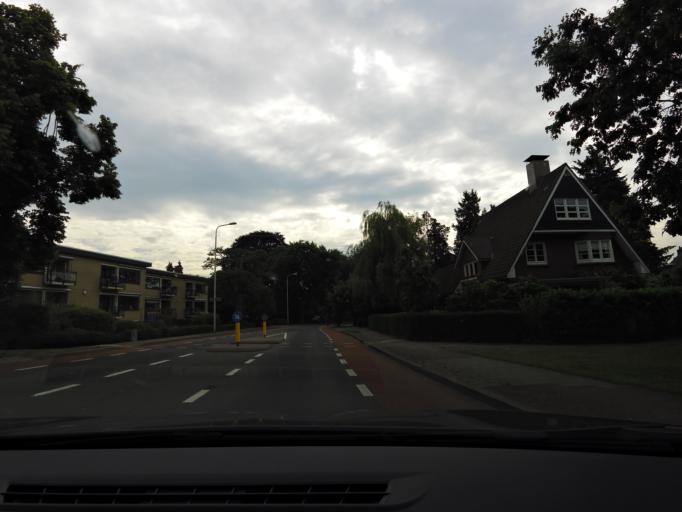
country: NL
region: Gelderland
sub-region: Gemeente Rheden
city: Velp
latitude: 52.0030
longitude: 5.9747
